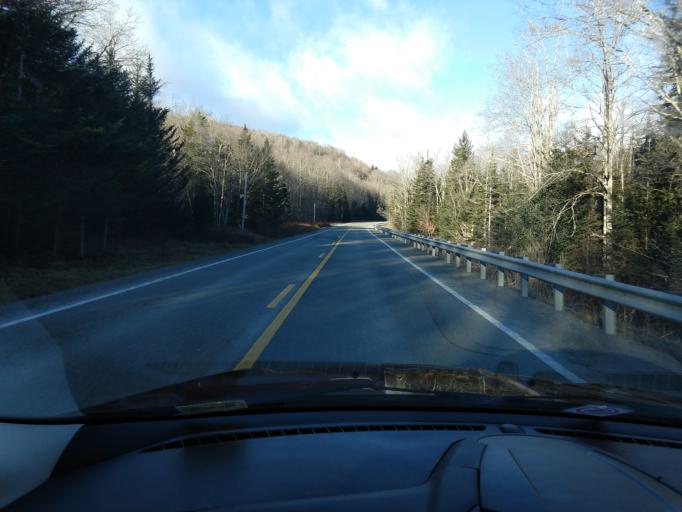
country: US
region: West Virginia
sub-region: Randolph County
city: Elkins
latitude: 38.6011
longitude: -79.8542
